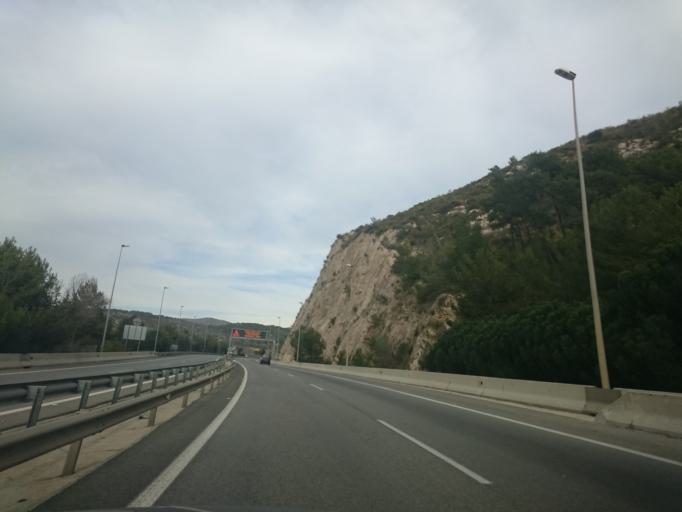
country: ES
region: Catalonia
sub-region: Provincia de Barcelona
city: Sitges
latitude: 41.2458
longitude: 1.8619
